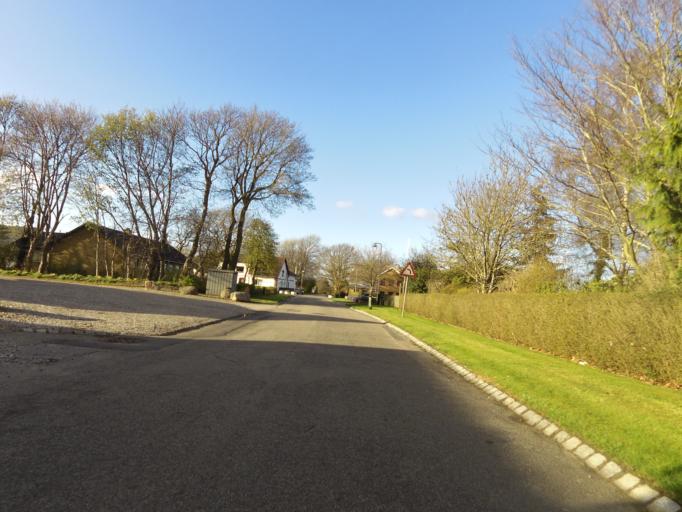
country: DK
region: South Denmark
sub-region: Tonder Kommune
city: Toftlund
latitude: 55.2331
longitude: 9.1244
